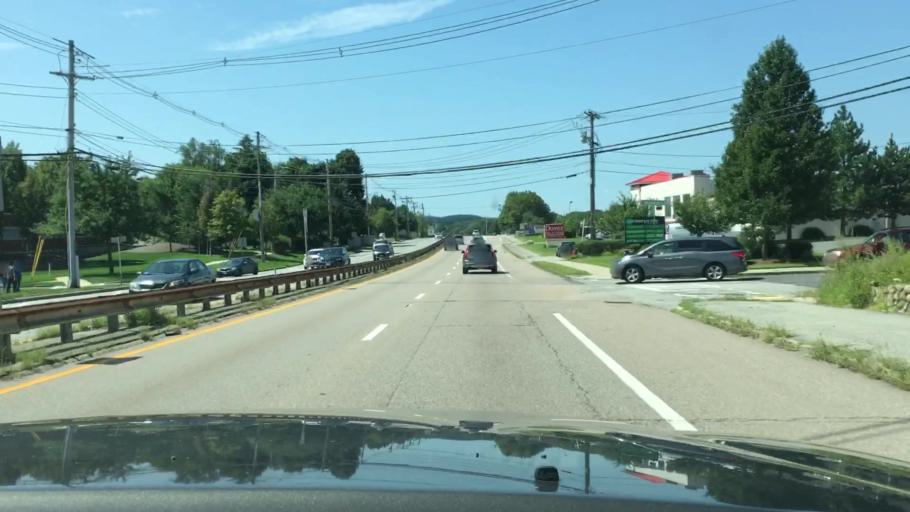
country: US
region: Massachusetts
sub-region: Middlesex County
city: Natick
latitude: 42.3009
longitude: -71.3521
